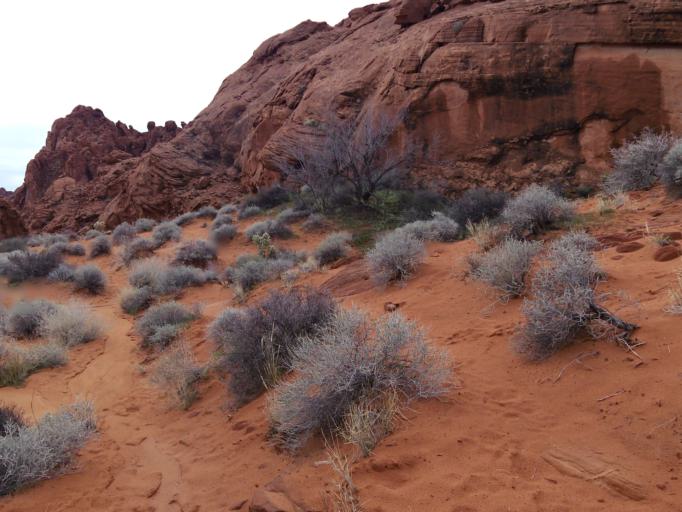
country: US
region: Nevada
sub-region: Clark County
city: Moapa Valley
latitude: 36.4495
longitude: -114.5116
